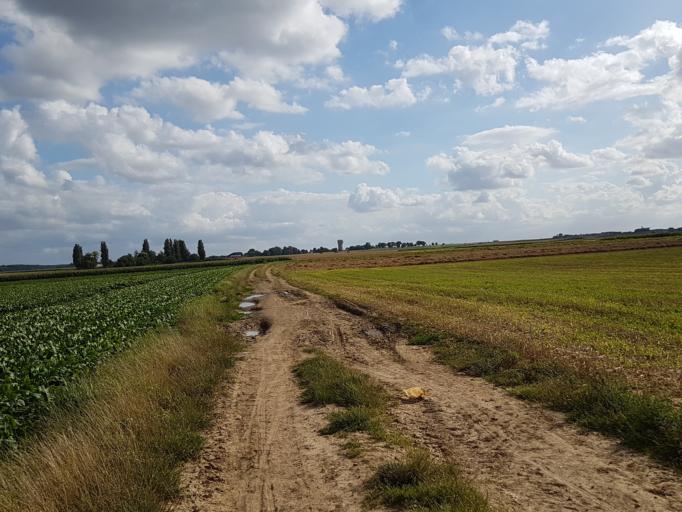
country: BE
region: Flanders
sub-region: Provincie Vlaams-Brabant
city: Kortenberg
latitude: 50.9113
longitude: 4.5409
